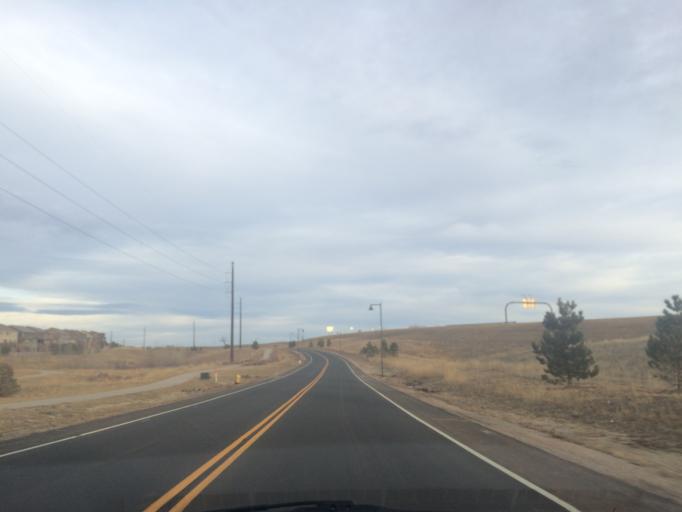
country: US
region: Colorado
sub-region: Boulder County
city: Lafayette
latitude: 39.9837
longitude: -105.0330
